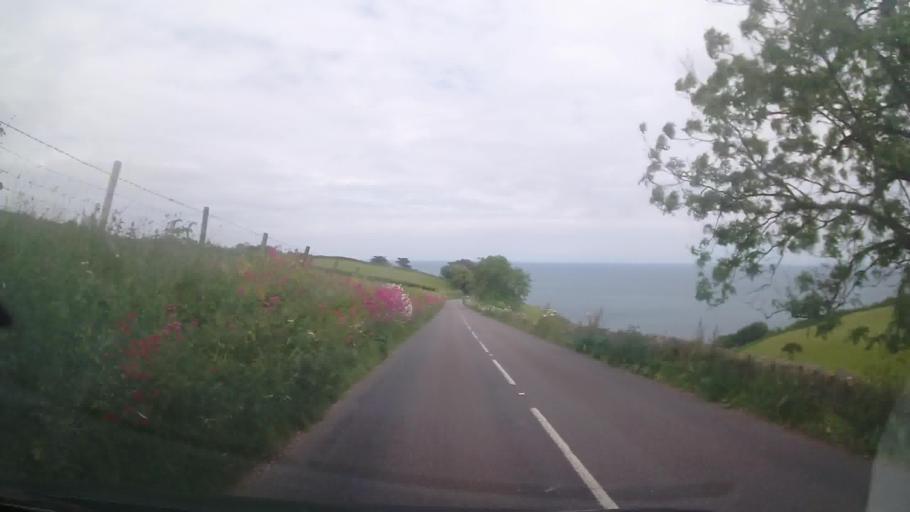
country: GB
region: England
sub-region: Devon
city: Dartmouth
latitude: 50.3154
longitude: -3.6227
